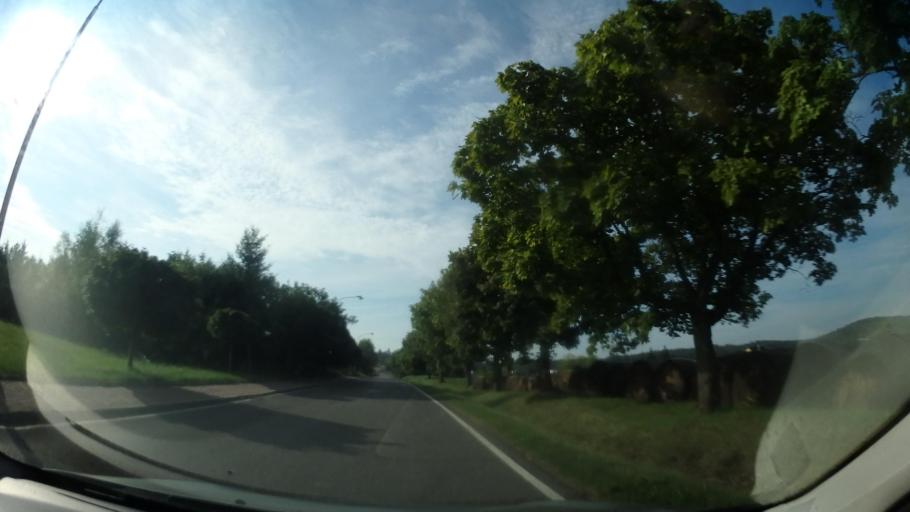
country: CZ
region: Jihocesky
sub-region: Okres Pisek
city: Pisek
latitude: 49.3873
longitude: 14.1274
